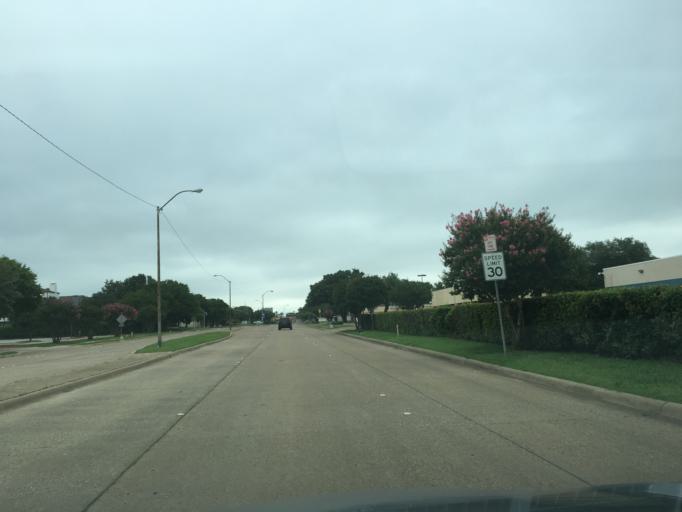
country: US
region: Texas
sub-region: Dallas County
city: Richardson
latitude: 32.9365
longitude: -96.7421
